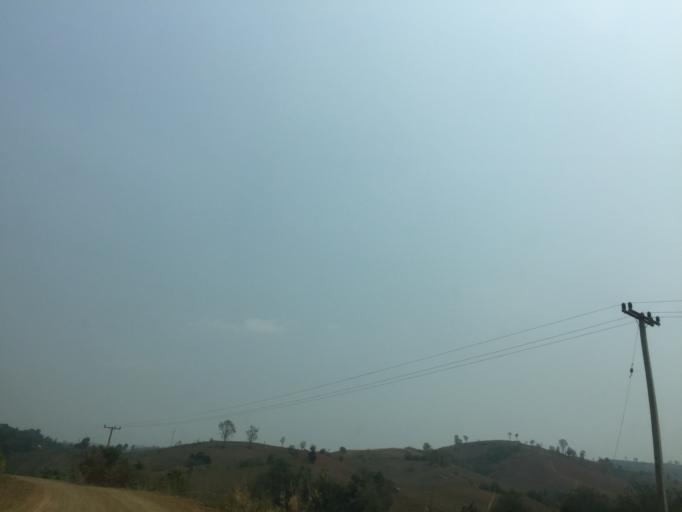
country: LA
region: Xiagnabouli
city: Muang Kenthao
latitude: 17.8093
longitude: 101.2701
